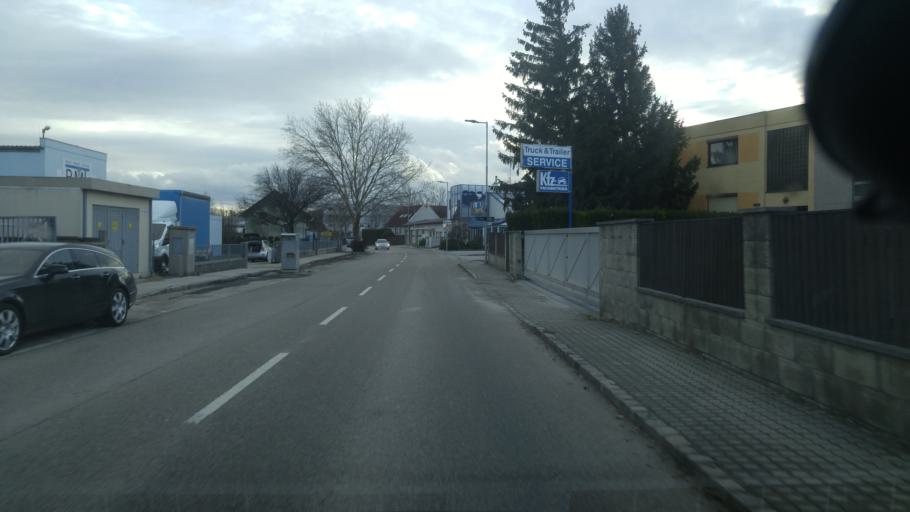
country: AT
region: Lower Austria
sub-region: Politischer Bezirk Baden
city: Bad Voslau
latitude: 47.9739
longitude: 16.2217
